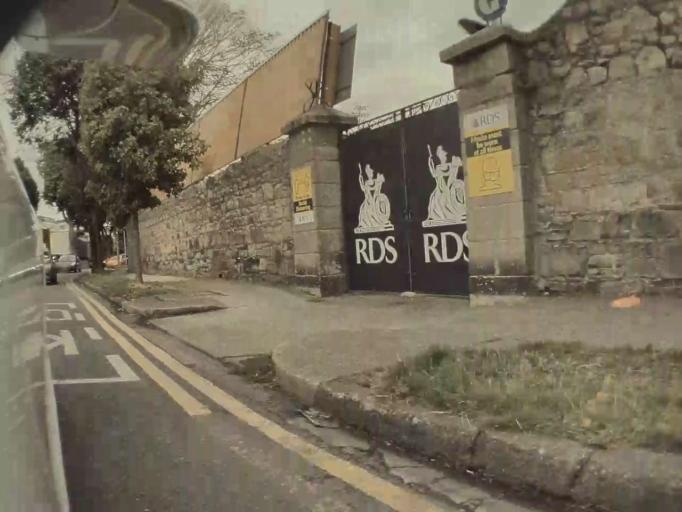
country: IE
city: Clonskeagh
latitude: 53.3255
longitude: -6.2312
